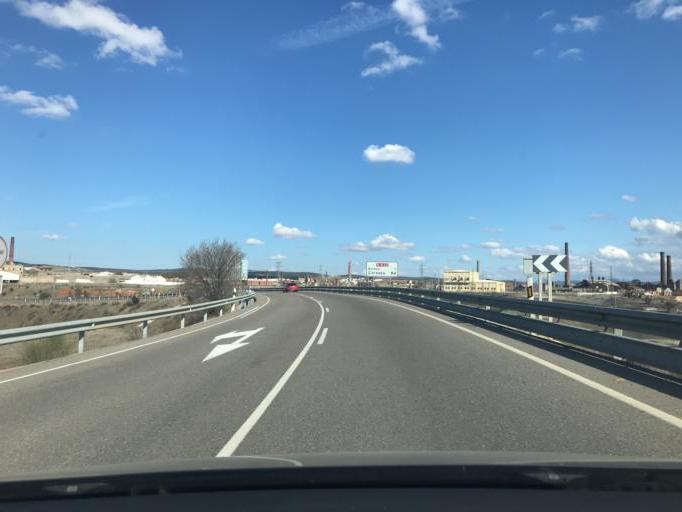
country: ES
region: Andalusia
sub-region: Province of Cordoba
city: Penarroya-Pueblonuevo
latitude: 38.2943
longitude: -5.2821
